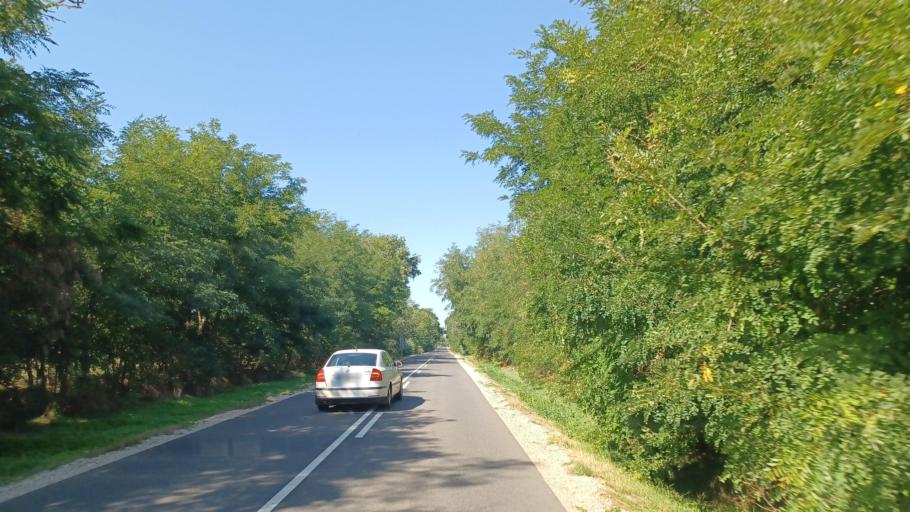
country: HU
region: Fejer
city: Alap
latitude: 46.7497
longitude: 18.6817
